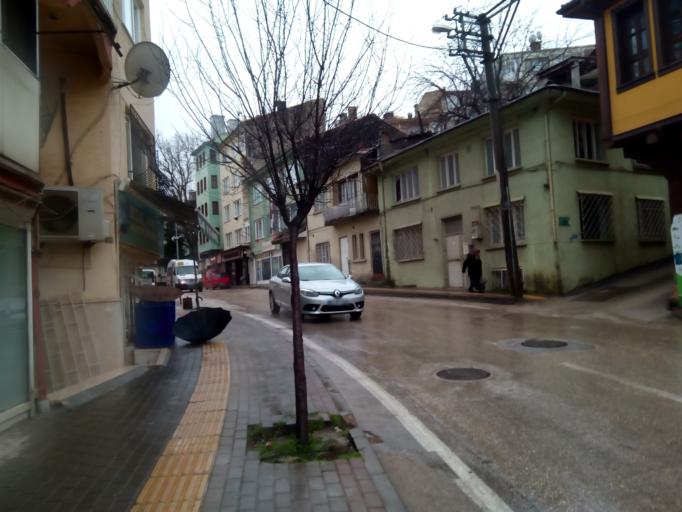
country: TR
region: Bursa
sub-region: Osmangazi
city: Bursa
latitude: 40.1775
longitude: 29.0612
